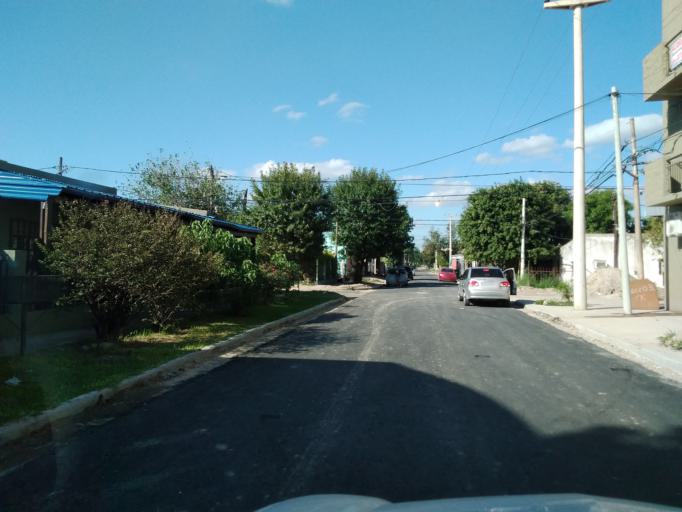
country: AR
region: Corrientes
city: Corrientes
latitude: -27.4635
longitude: -58.7836
